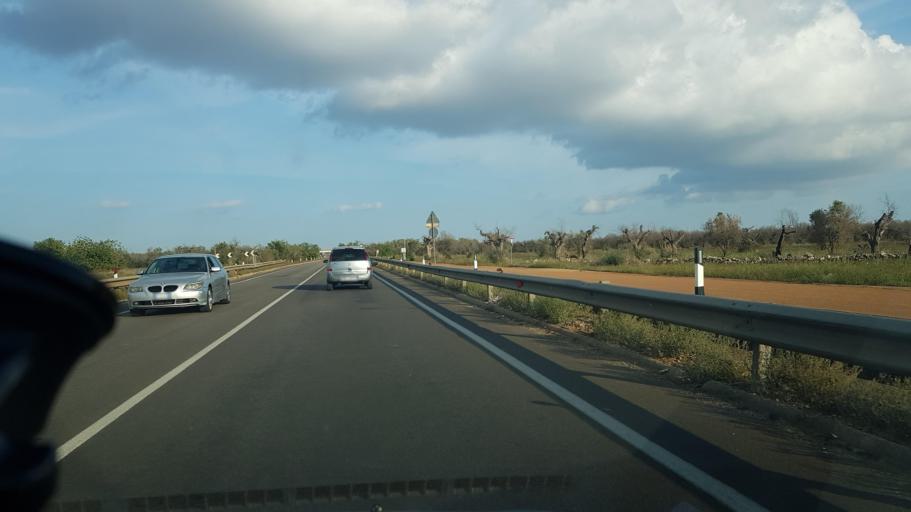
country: IT
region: Apulia
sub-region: Provincia di Lecce
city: Gemini
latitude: 39.9191
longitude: 18.2102
